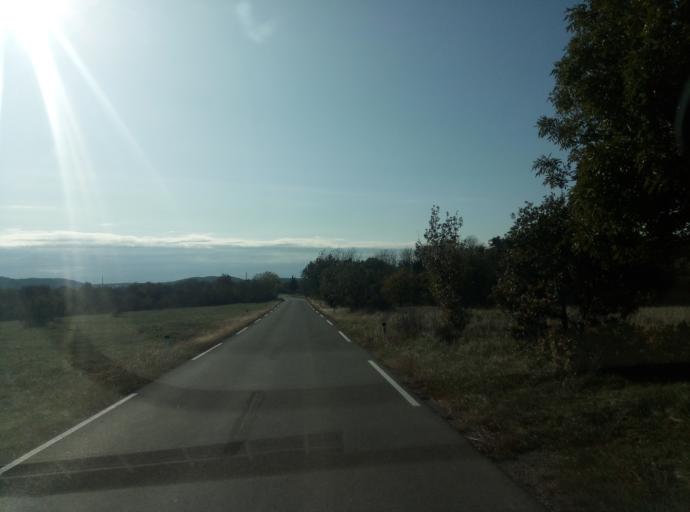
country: SI
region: Komen
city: Komen
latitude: 45.8086
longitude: 13.7259
